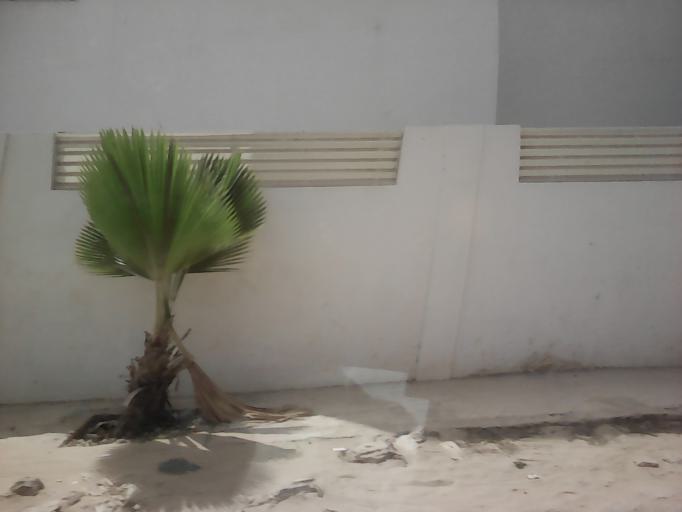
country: SN
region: Dakar
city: Grand Dakar
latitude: 14.7336
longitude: -17.4322
